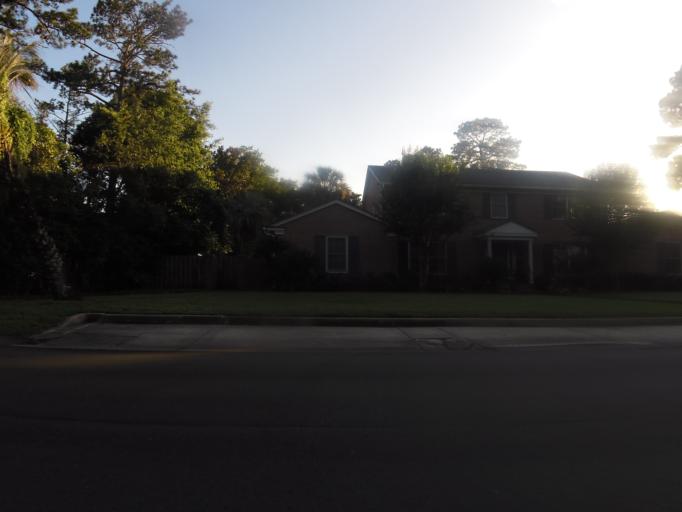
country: US
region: Florida
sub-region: Duval County
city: Jacksonville
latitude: 30.2546
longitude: -81.6911
